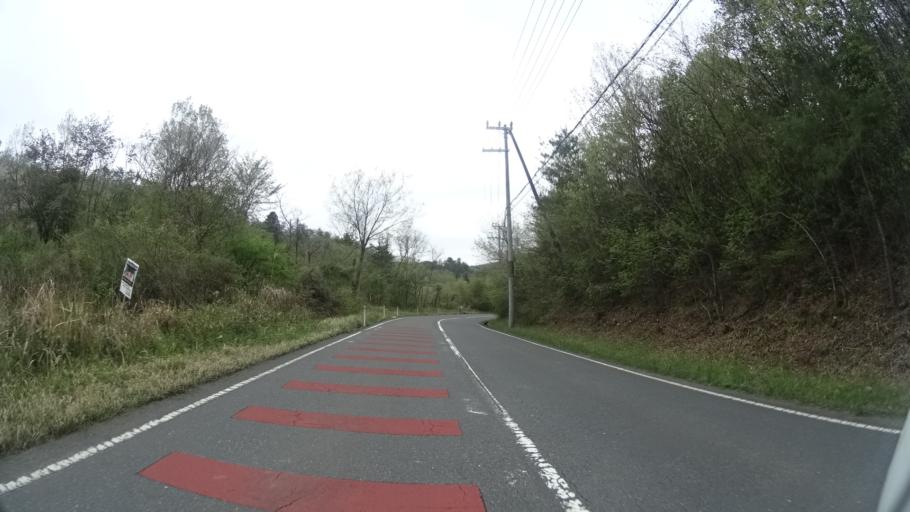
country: JP
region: Kyoto
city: Kameoka
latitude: 35.1835
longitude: 135.4530
